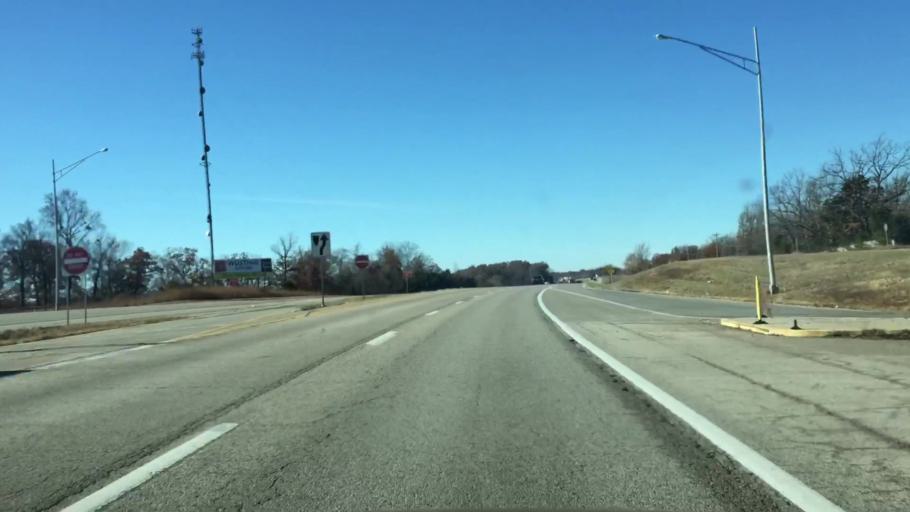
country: US
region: Missouri
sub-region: Cole County
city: Wardsville
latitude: 38.4735
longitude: -92.2788
